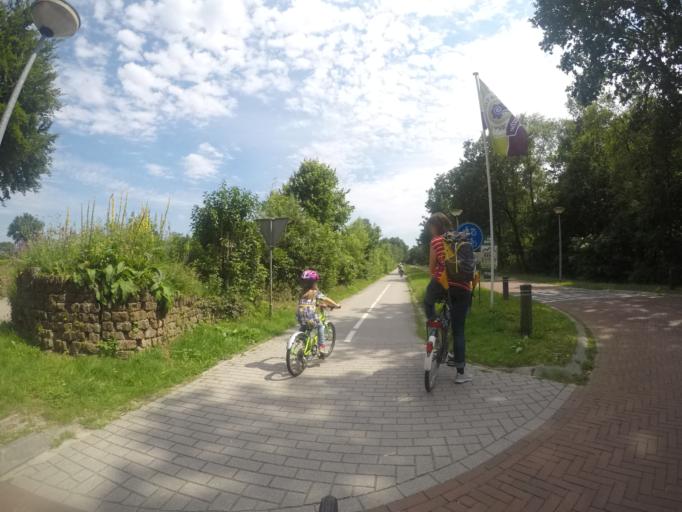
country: NL
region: Drenthe
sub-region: Gemeente Westerveld
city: Dwingeloo
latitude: 52.8903
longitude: 6.3129
